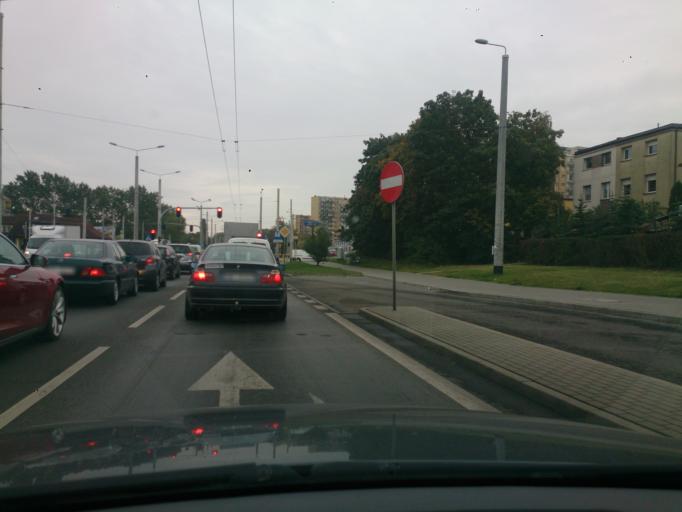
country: PL
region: Pomeranian Voivodeship
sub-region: Gdynia
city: Pogorze
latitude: 54.5466
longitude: 18.4398
